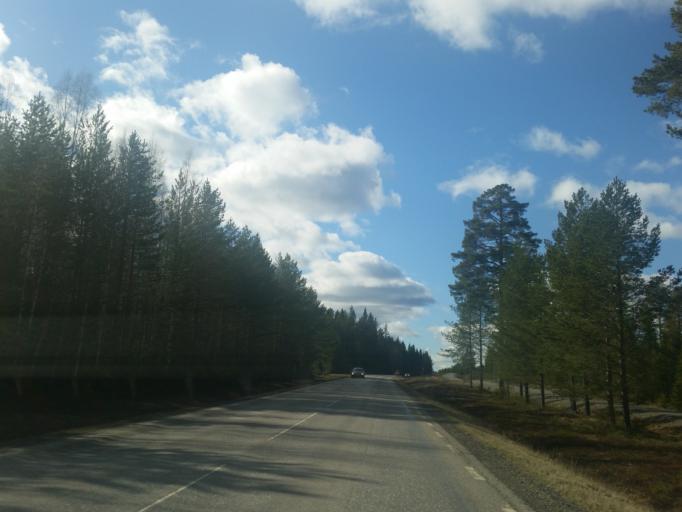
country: SE
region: Vaesterbotten
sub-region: Robertsfors Kommun
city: Robertsfors
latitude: 64.1765
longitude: 20.9054
